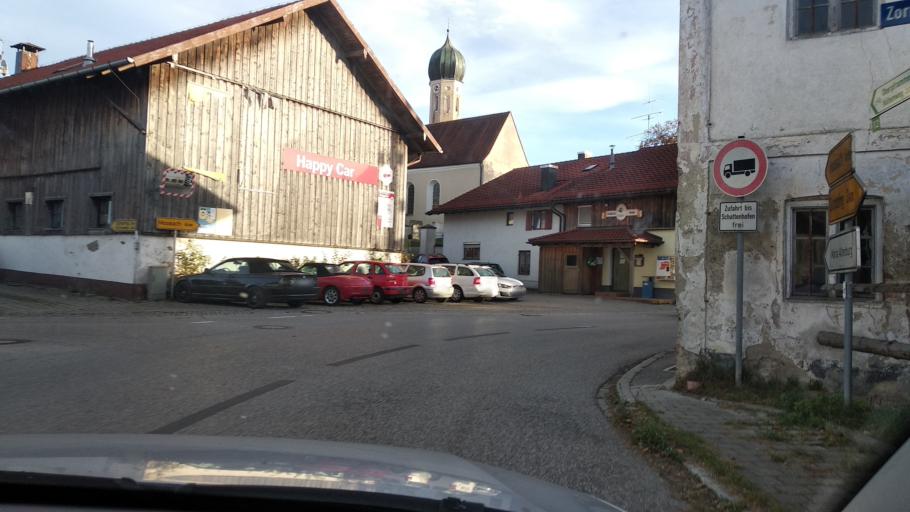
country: DE
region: Bavaria
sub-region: Upper Bavaria
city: Zorneding
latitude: 48.0609
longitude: 11.8507
